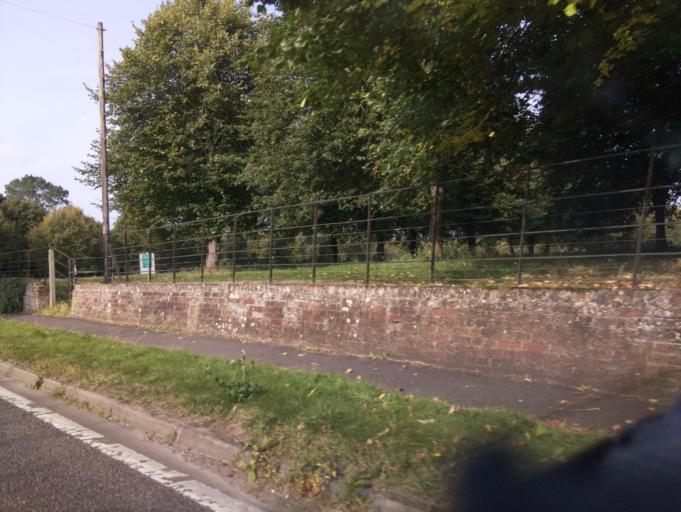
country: GB
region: England
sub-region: Warwickshire
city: Studley
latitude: 52.2424
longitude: -1.8842
